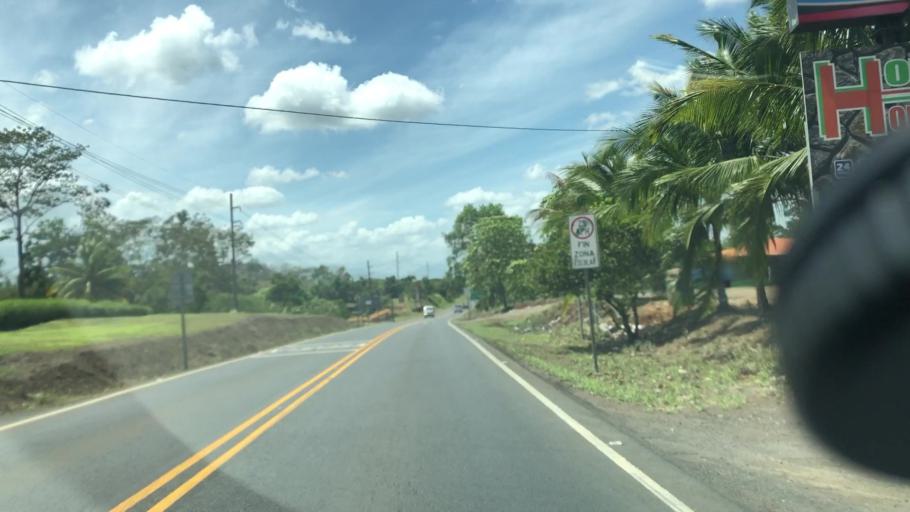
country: CR
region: Alajuela
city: Quesada
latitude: 10.4566
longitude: -84.4081
